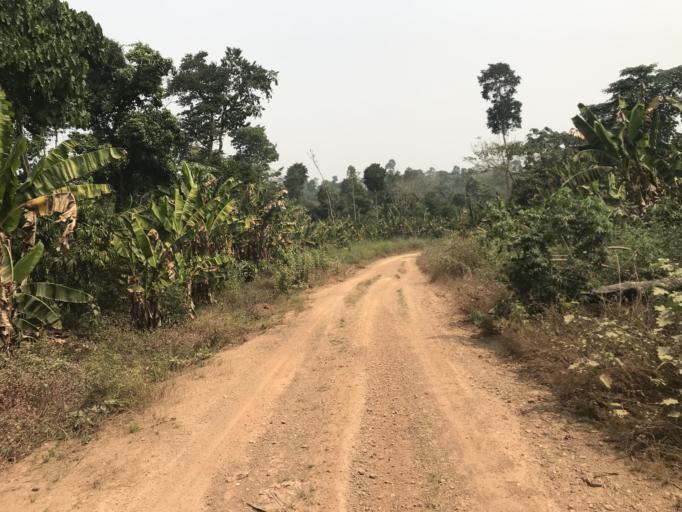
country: NG
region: Osun
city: Ifetedo
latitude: 7.0508
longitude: 4.4758
